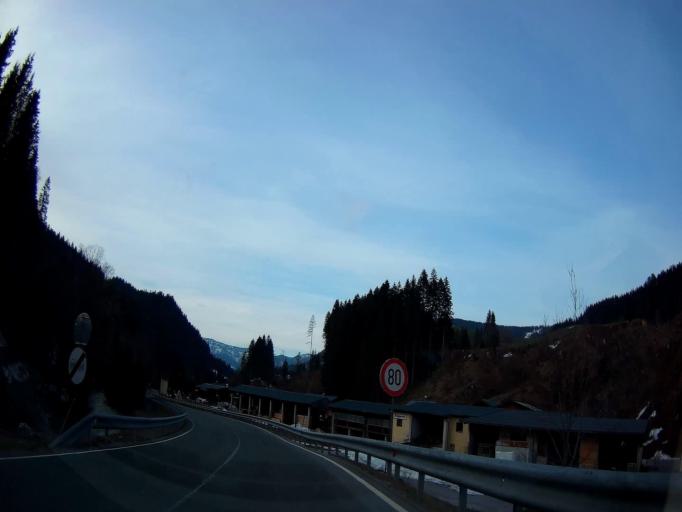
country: AT
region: Salzburg
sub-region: Politischer Bezirk Hallein
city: Abtenau
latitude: 47.5322
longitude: 13.4249
